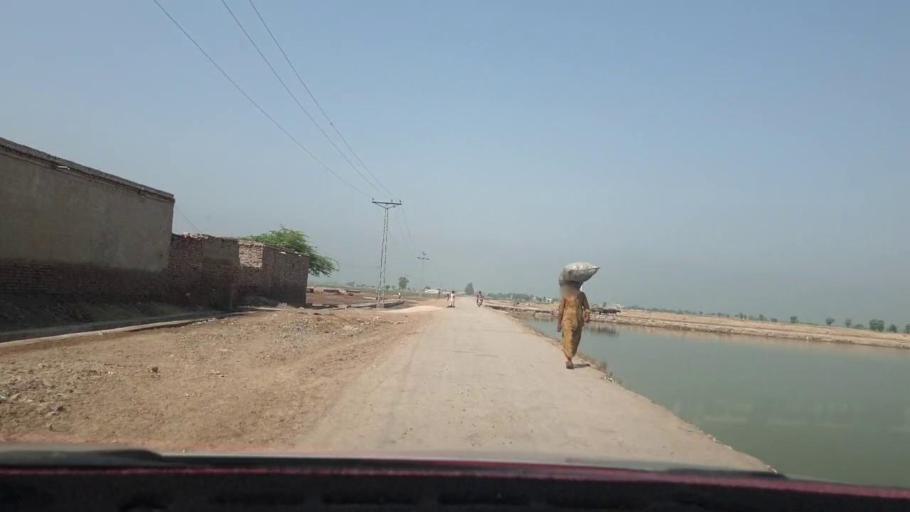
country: PK
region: Sindh
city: Nasirabad
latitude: 27.4249
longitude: 67.9235
